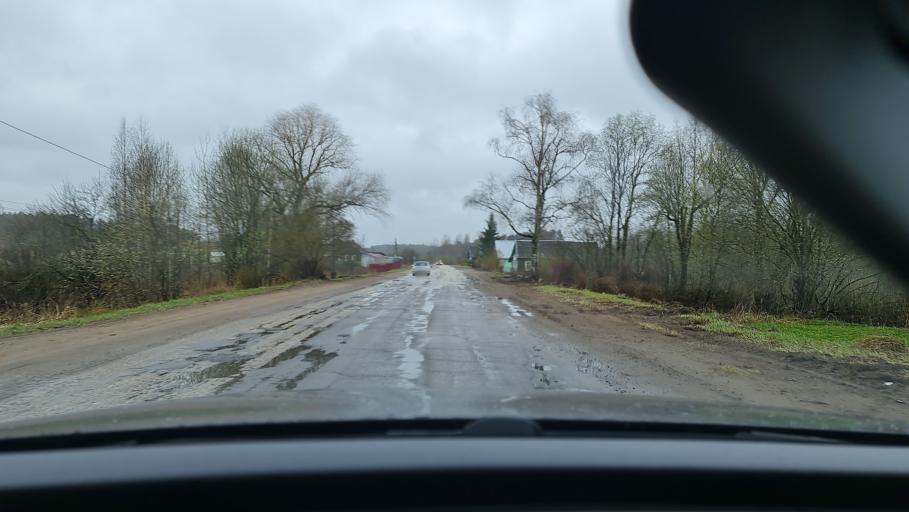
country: RU
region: Novgorod
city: Valday
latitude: 58.0362
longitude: 32.9433
